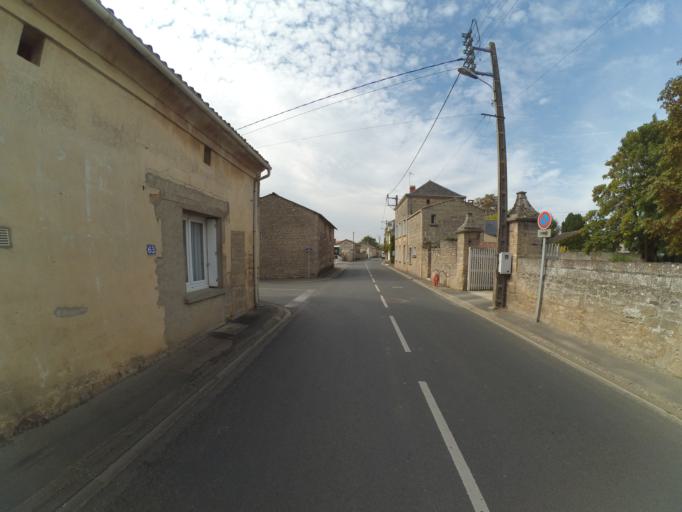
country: FR
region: Pays de la Loire
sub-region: Departement de Maine-et-Loire
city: Doue-la-Fontaine
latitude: 47.1938
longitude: -0.3068
